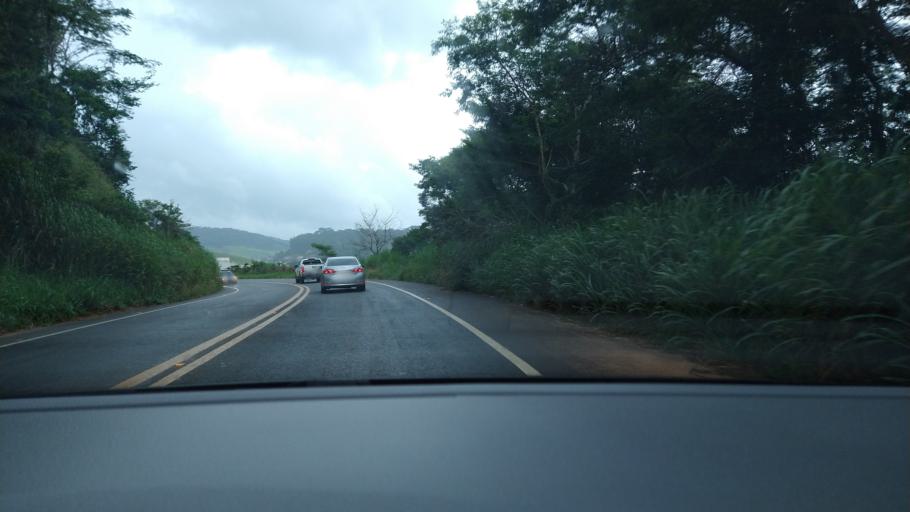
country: BR
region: Minas Gerais
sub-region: Vicosa
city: Vicosa
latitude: -20.6500
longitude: -42.8603
